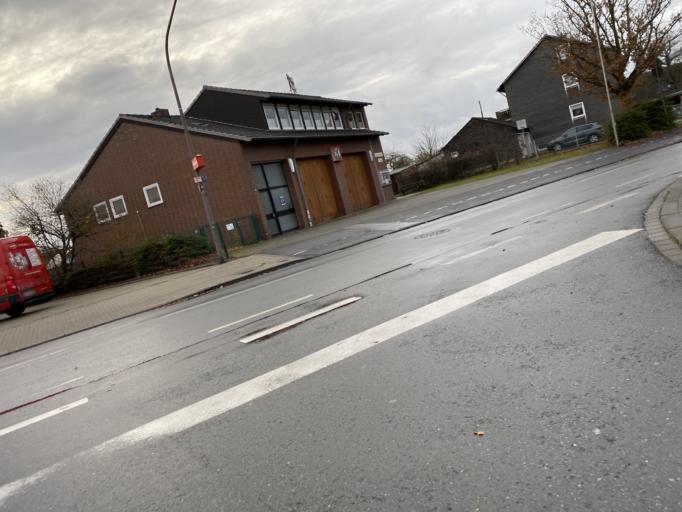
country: DE
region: North Rhine-Westphalia
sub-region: Regierungsbezirk Arnsberg
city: Hamm
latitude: 51.6823
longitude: 7.8609
